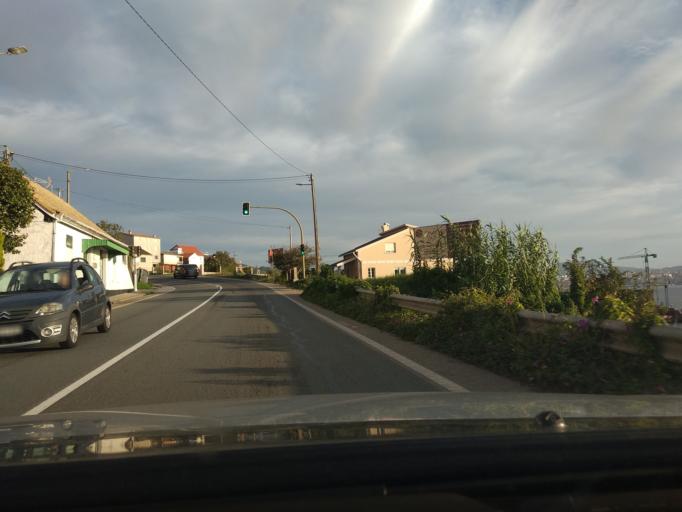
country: ES
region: Galicia
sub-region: Provincia de Pontevedra
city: Moana
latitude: 42.2823
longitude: -8.7131
